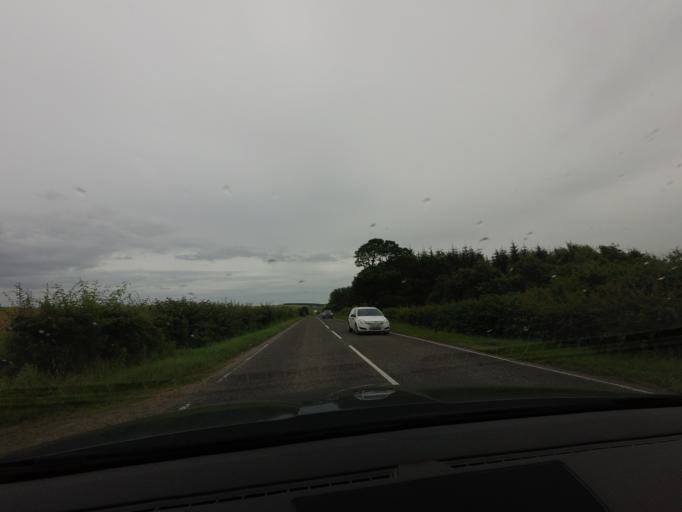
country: GB
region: Scotland
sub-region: Moray
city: Cullen
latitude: 57.6782
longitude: -2.7624
